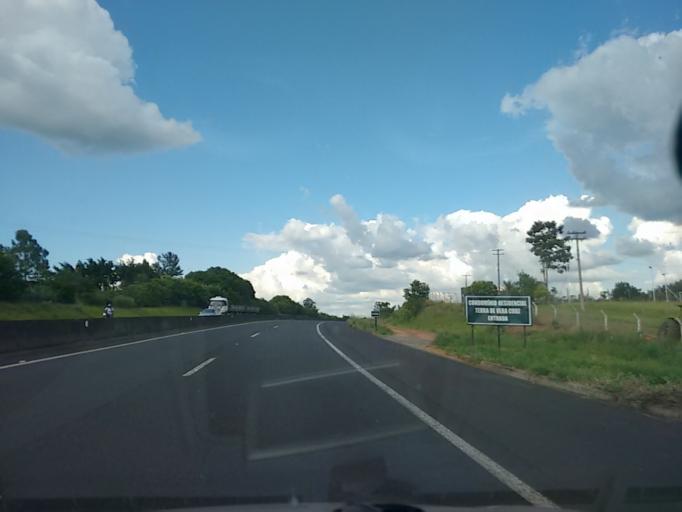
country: BR
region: Sao Paulo
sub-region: Marilia
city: Marilia
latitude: -22.2276
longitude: -49.8053
